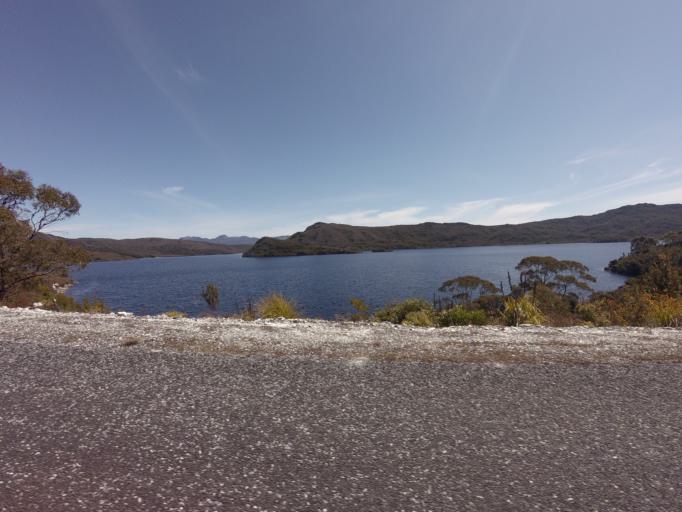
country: AU
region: Tasmania
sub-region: Huon Valley
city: Geeveston
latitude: -42.8351
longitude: 146.1273
